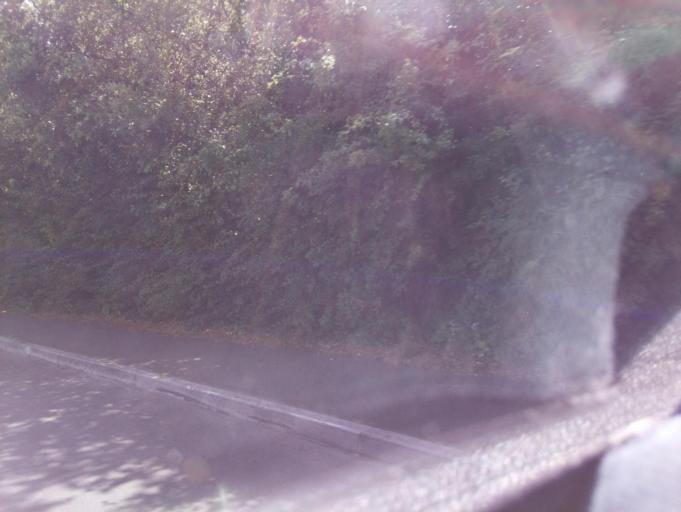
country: GB
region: Wales
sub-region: Caerphilly County Borough
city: Pengam
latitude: 51.6605
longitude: -3.2281
